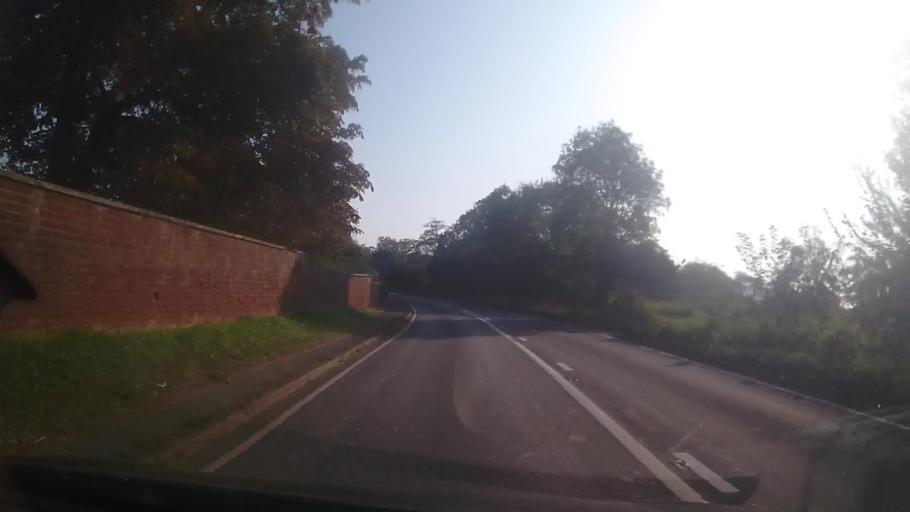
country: GB
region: England
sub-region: Shropshire
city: Berrington
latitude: 52.6798
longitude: -2.6668
